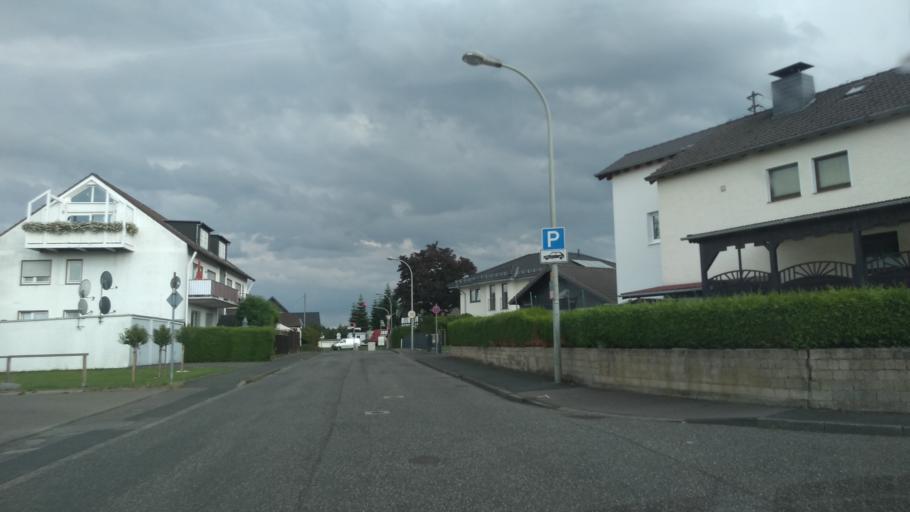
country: DE
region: North Rhine-Westphalia
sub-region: Regierungsbezirk Koln
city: Hennef
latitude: 50.8329
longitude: 7.2824
